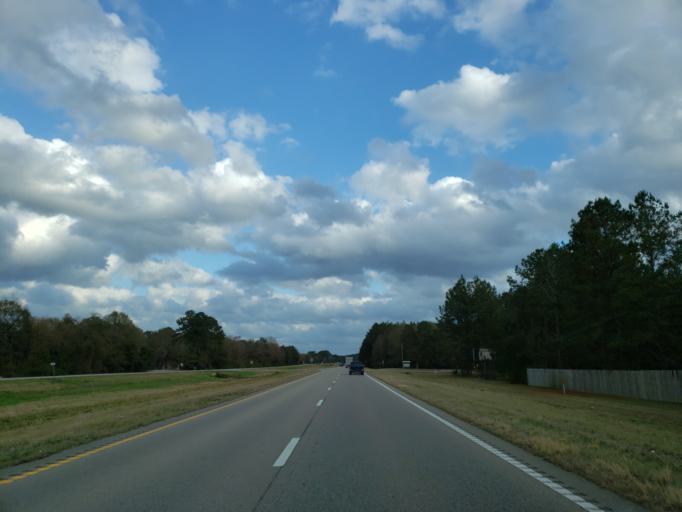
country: US
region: Mississippi
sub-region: Forrest County
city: Petal
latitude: 31.2331
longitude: -89.2026
